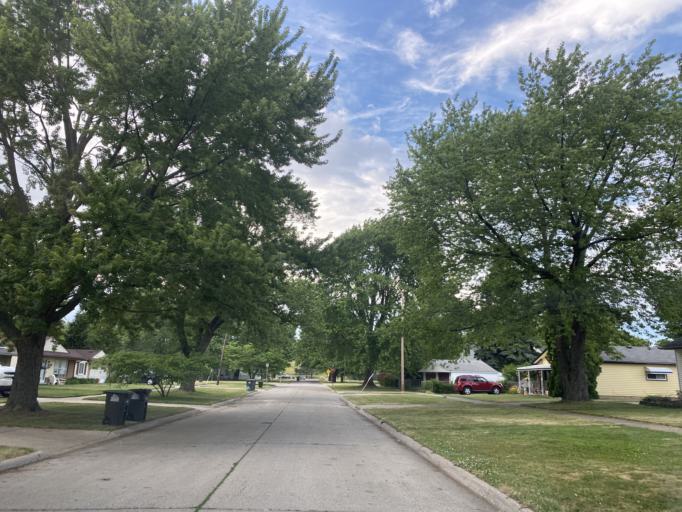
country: US
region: Michigan
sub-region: Wayne County
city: Allen Park
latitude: 42.2577
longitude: -83.2408
